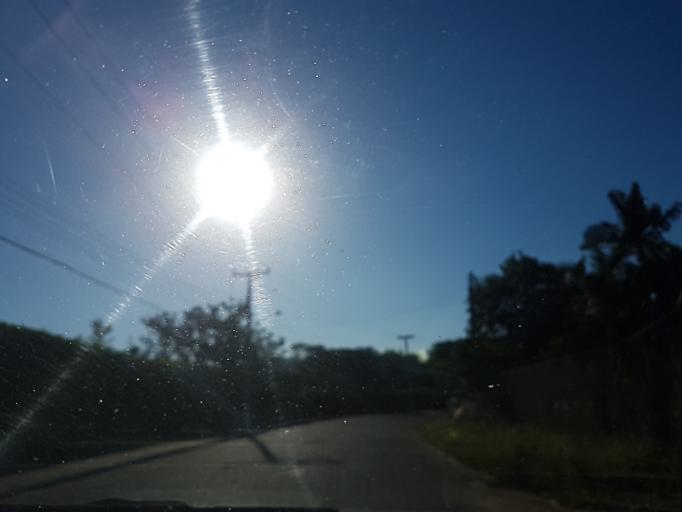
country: BR
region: Santa Catarina
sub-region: Braco Do Norte
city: Braco do Norte
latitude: -28.3303
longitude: -49.1714
